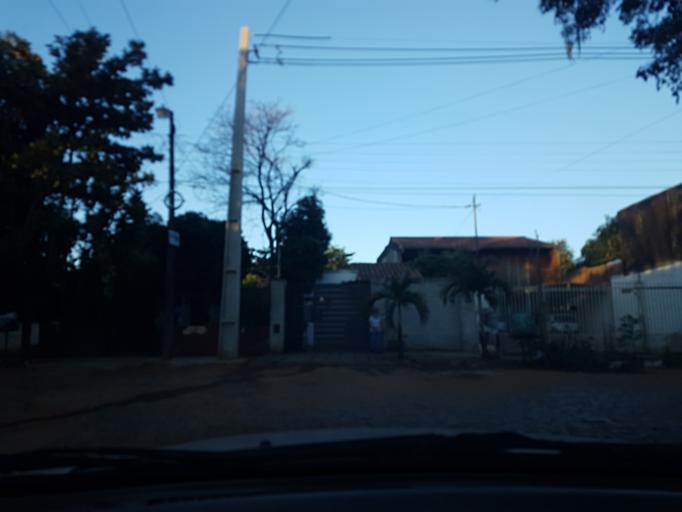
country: PY
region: Asuncion
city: Asuncion
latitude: -25.2703
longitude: -57.5687
